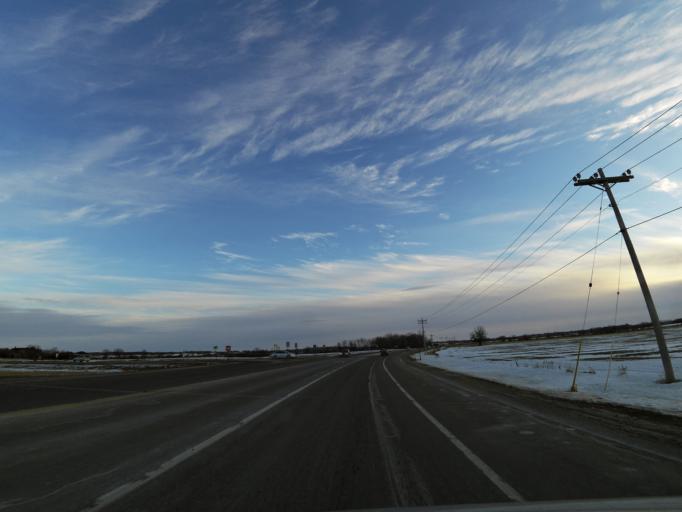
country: US
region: Minnesota
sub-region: Washington County
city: Lake Elmo
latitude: 45.0078
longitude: -92.8633
